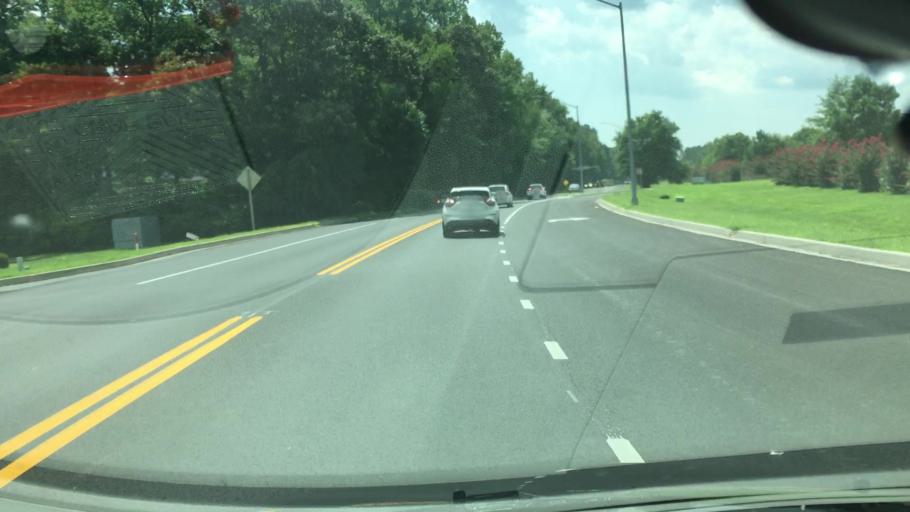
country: US
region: Maryland
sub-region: Worcester County
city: Ocean Pines
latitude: 38.3745
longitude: -75.1632
